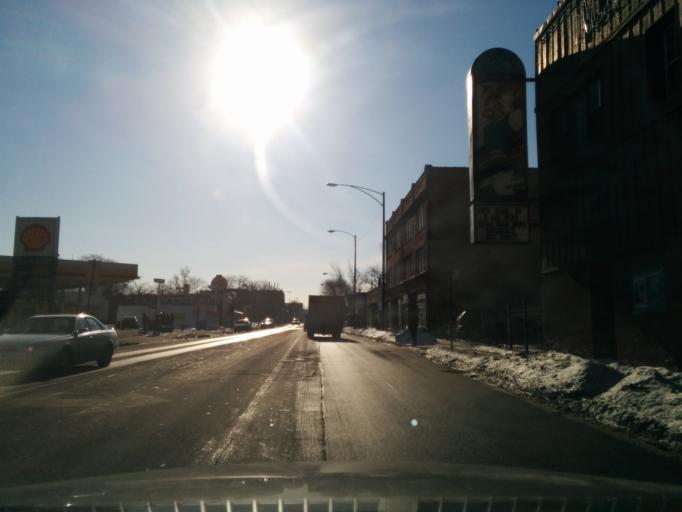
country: US
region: Illinois
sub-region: Cook County
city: Lincolnwood
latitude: 41.9391
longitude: -87.7241
